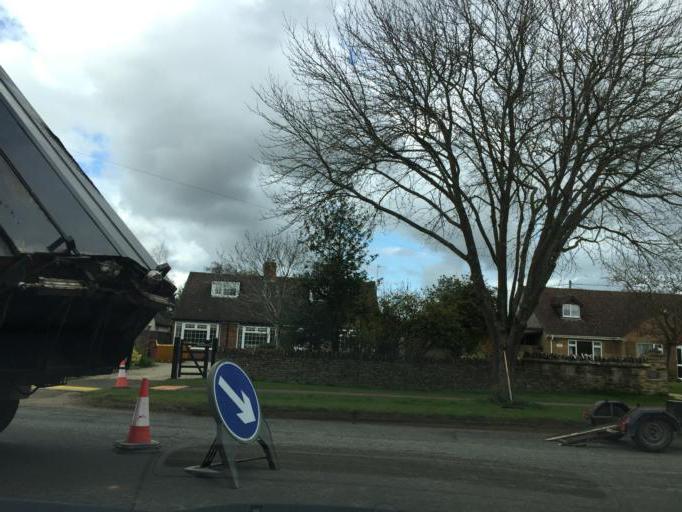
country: GB
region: England
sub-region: Oxfordshire
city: Stonesfield
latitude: 51.8536
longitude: -1.4295
